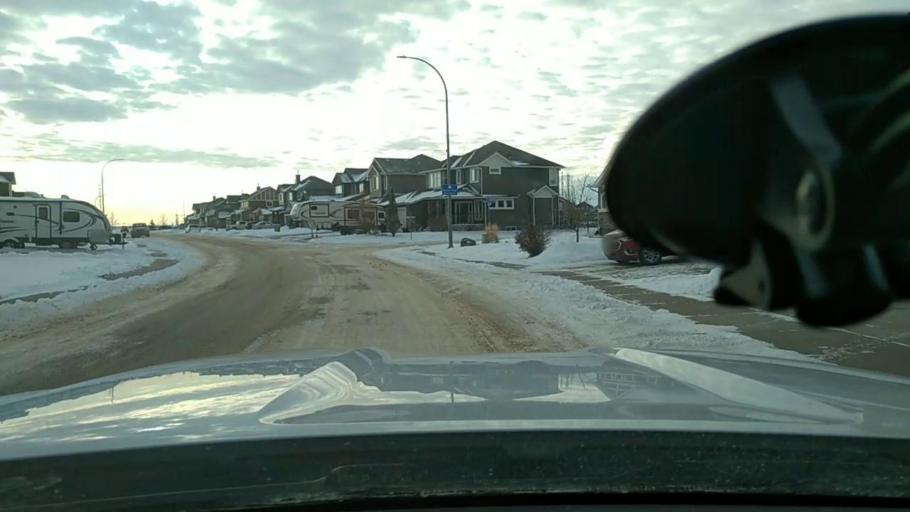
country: CA
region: Alberta
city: Chestermere
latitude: 50.9629
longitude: -113.6628
